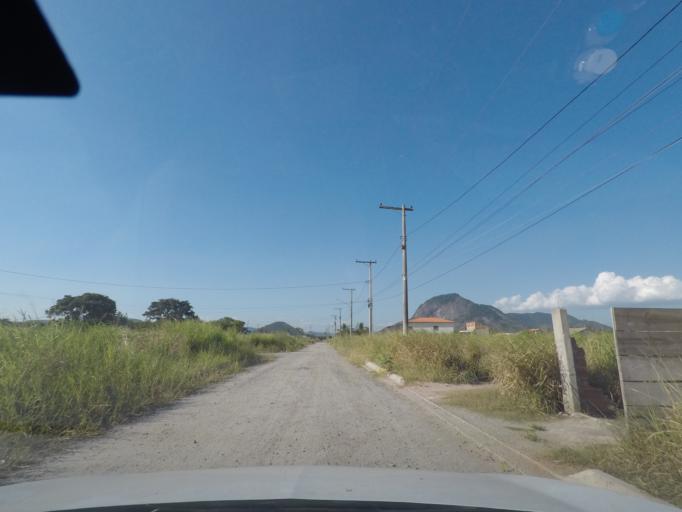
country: BR
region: Rio de Janeiro
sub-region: Marica
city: Marica
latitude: -22.9612
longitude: -42.9253
